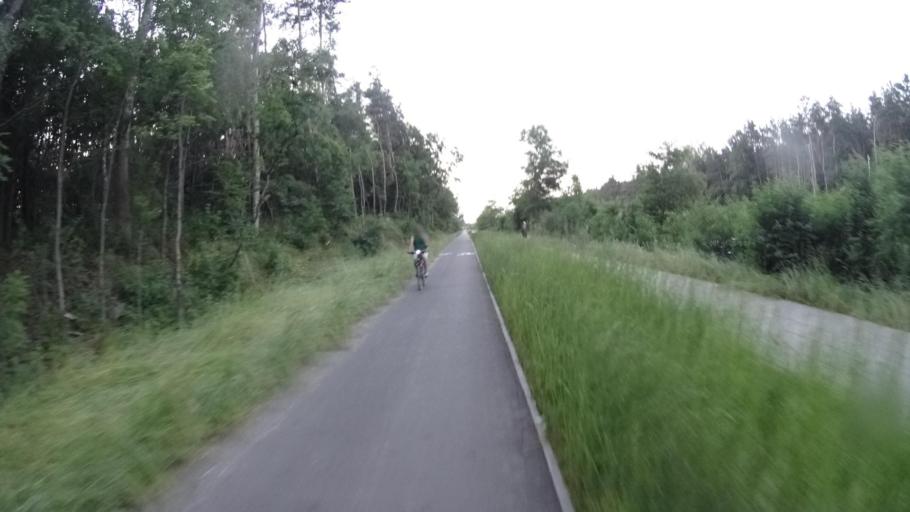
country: PL
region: Masovian Voivodeship
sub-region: Powiat legionowski
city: Stanislawow Pierwszy
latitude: 52.3678
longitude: 21.0329
